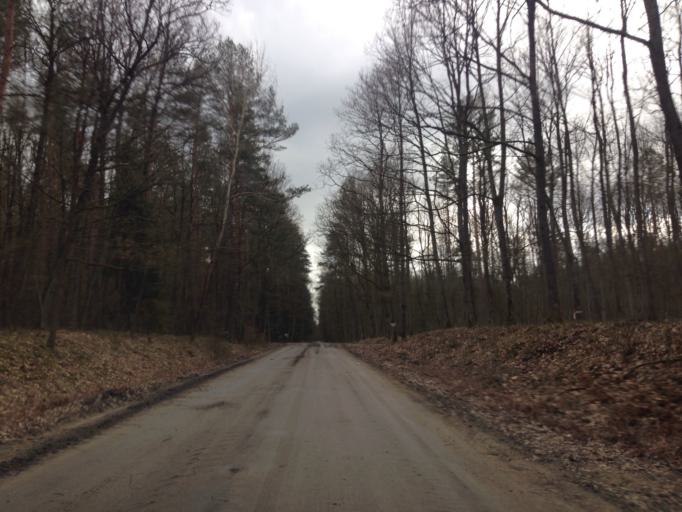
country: PL
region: Kujawsko-Pomorskie
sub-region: Powiat brodnicki
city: Gorzno
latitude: 53.1982
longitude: 19.6942
